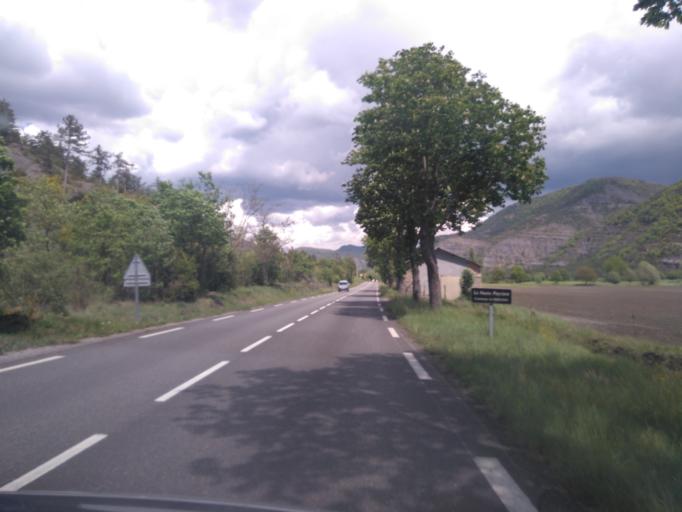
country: FR
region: Provence-Alpes-Cote d'Azur
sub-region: Departement des Alpes-de-Haute-Provence
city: Digne-les-Bains
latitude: 44.1149
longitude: 6.2703
